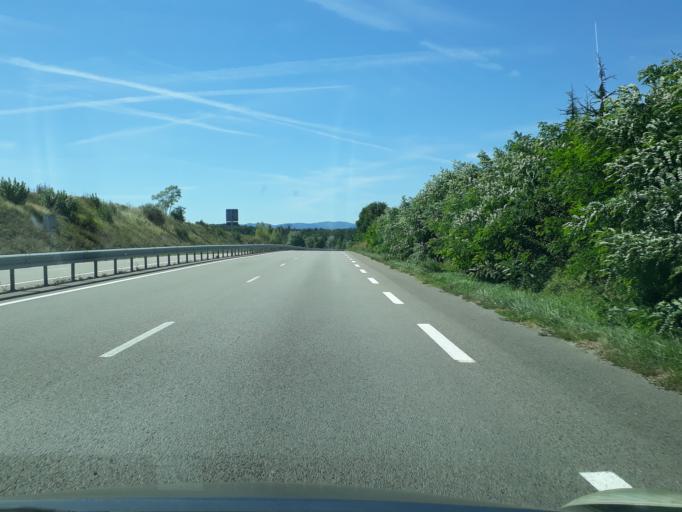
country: FR
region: Rhone-Alpes
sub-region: Departement de l'Ardeche
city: Peaugres
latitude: 45.2745
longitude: 4.7198
